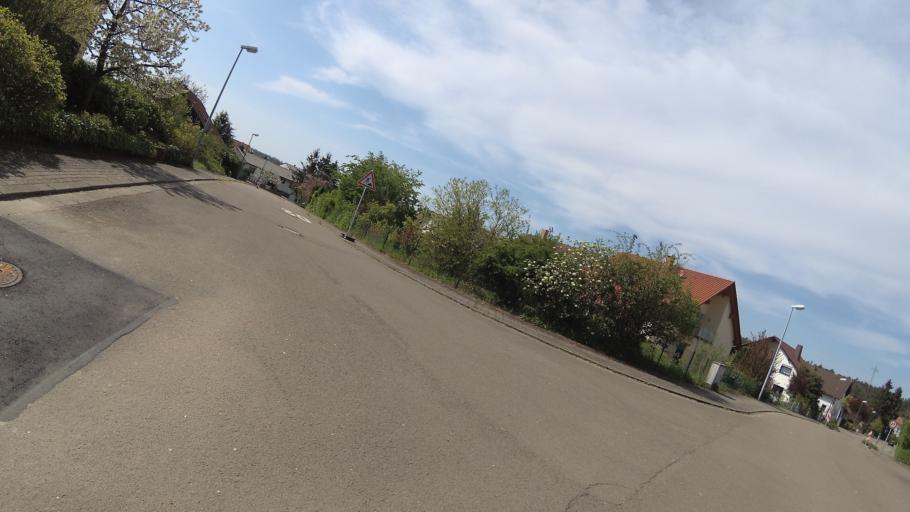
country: DE
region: Saarland
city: Homburg
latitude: 49.3456
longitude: 7.3363
